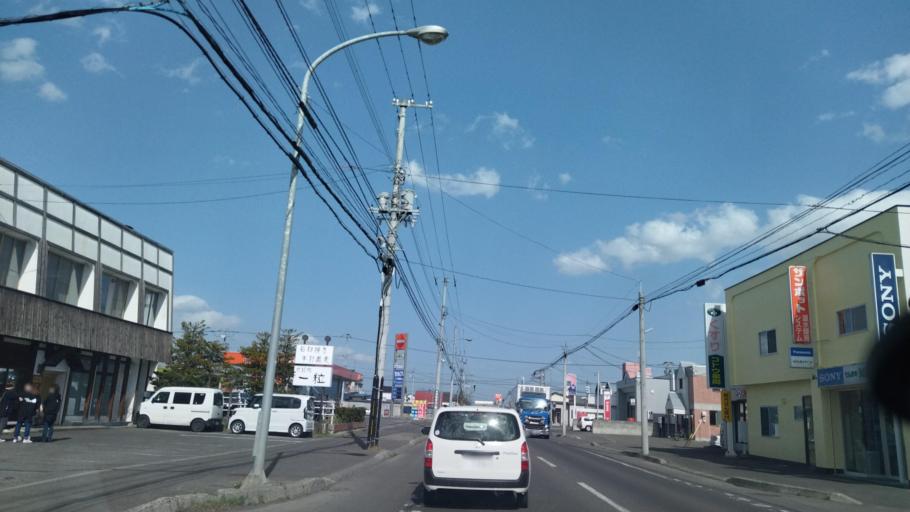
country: JP
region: Hokkaido
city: Obihiro
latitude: 42.9345
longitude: 143.1682
